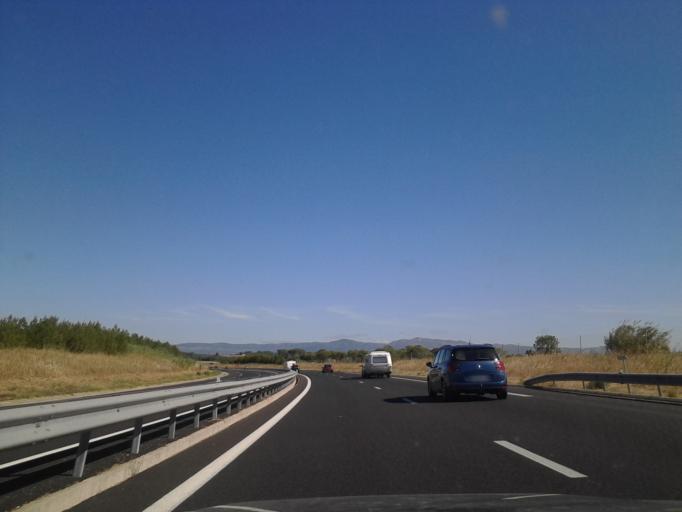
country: FR
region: Languedoc-Roussillon
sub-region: Departement de l'Herault
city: Aspiran
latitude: 43.5633
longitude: 3.4666
